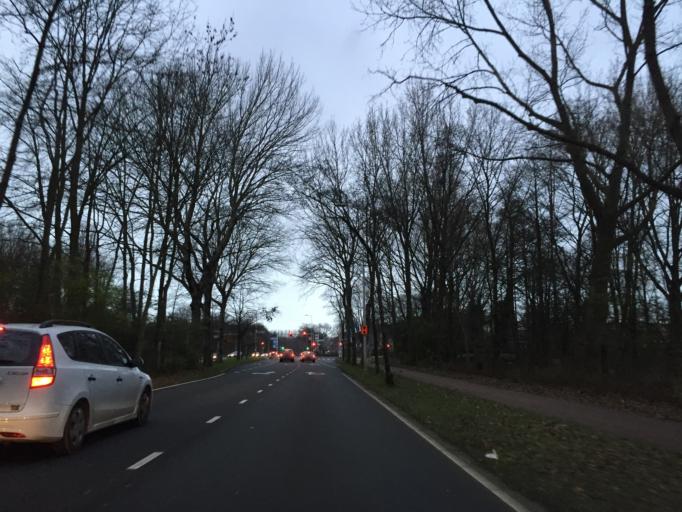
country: NL
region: South Holland
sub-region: Gemeente Westland
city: Poeldijk
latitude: 52.0507
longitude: 4.2303
